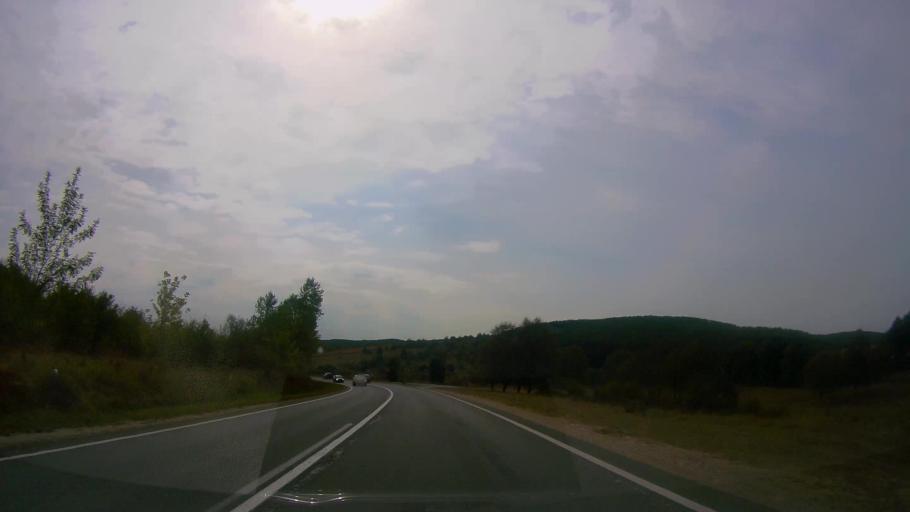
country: RO
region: Salaj
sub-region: Comuna Romanasi
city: Romanasi
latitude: 47.0604
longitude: 23.2139
